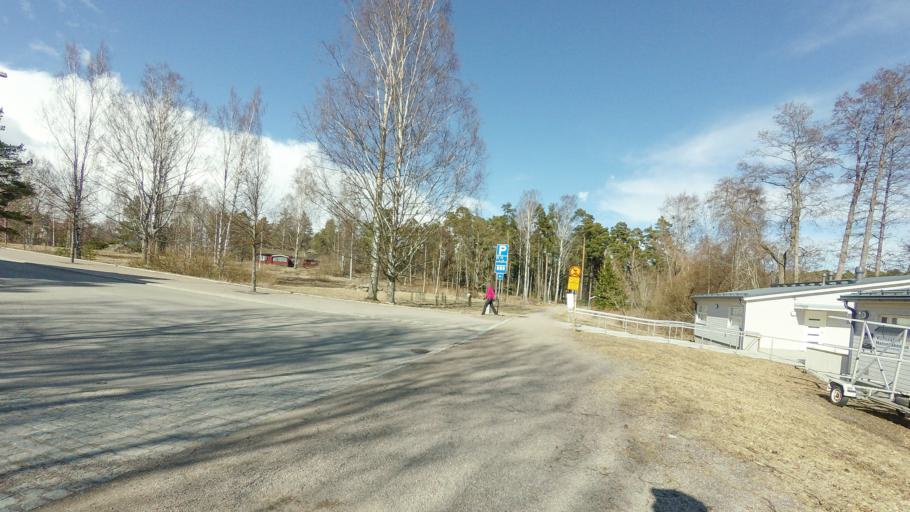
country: FI
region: Uusimaa
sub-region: Helsinki
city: Vantaa
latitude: 60.1978
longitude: 25.1279
